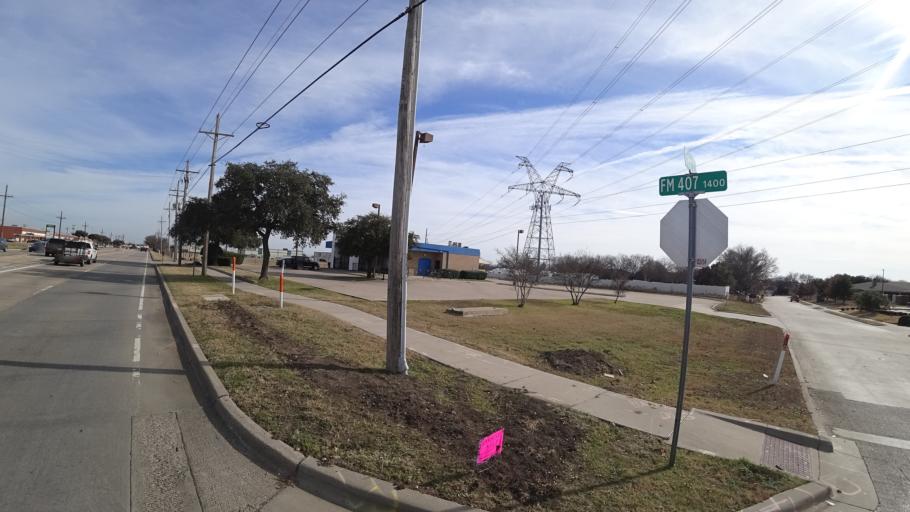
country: US
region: Texas
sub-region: Denton County
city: Highland Village
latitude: 33.0713
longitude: -97.0322
